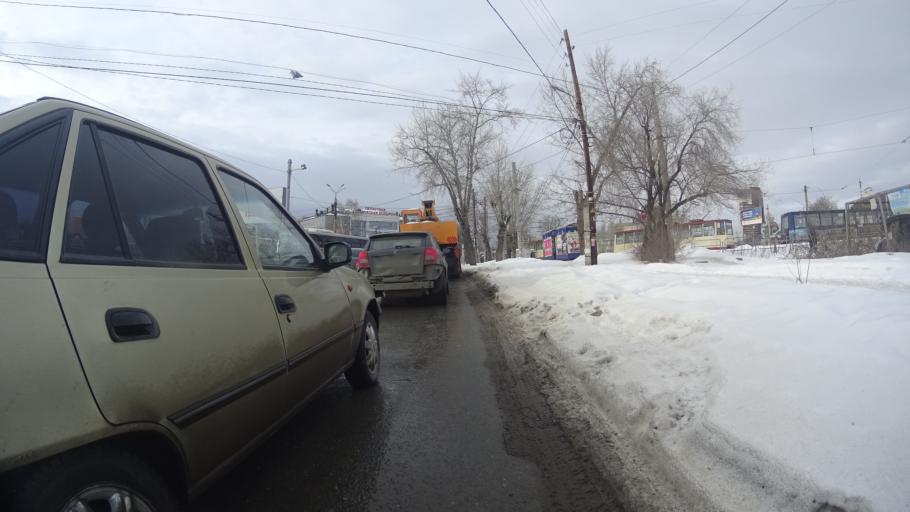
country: RU
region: Chelyabinsk
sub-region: Gorod Chelyabinsk
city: Chelyabinsk
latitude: 55.1359
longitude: 61.3761
